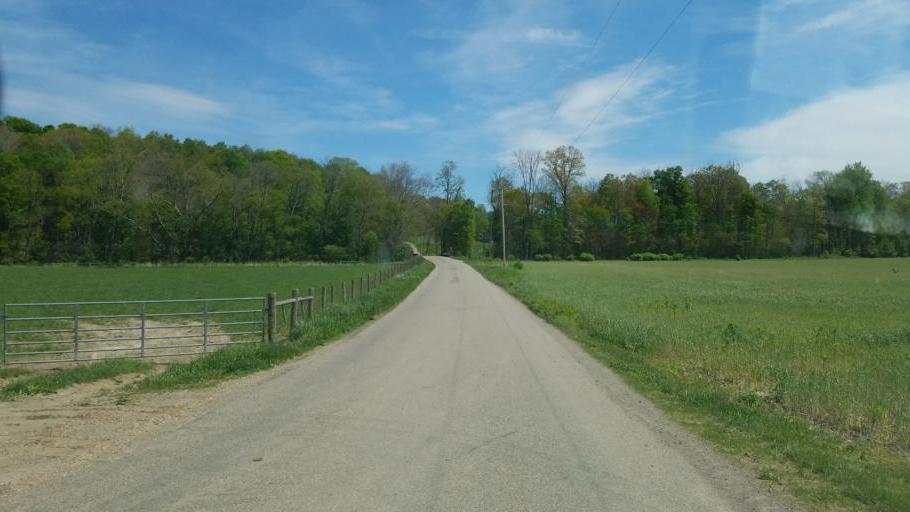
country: US
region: Ohio
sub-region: Knox County
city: Gambier
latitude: 40.4234
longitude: -82.3835
